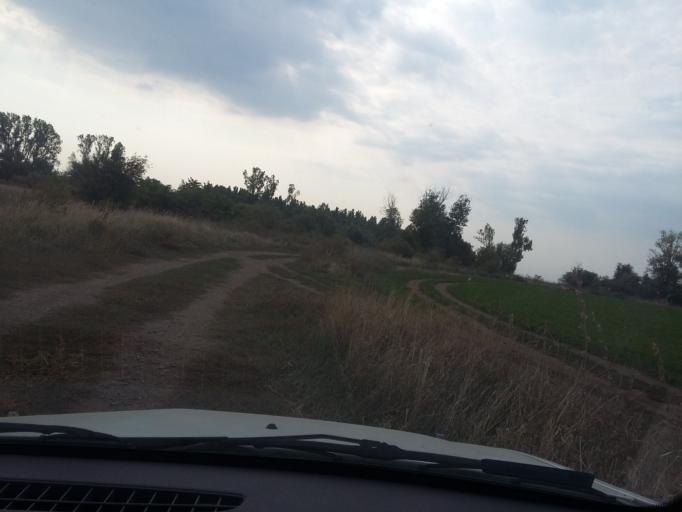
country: HU
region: Borsod-Abauj-Zemplen
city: Taktaszada
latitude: 48.1217
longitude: 21.2050
